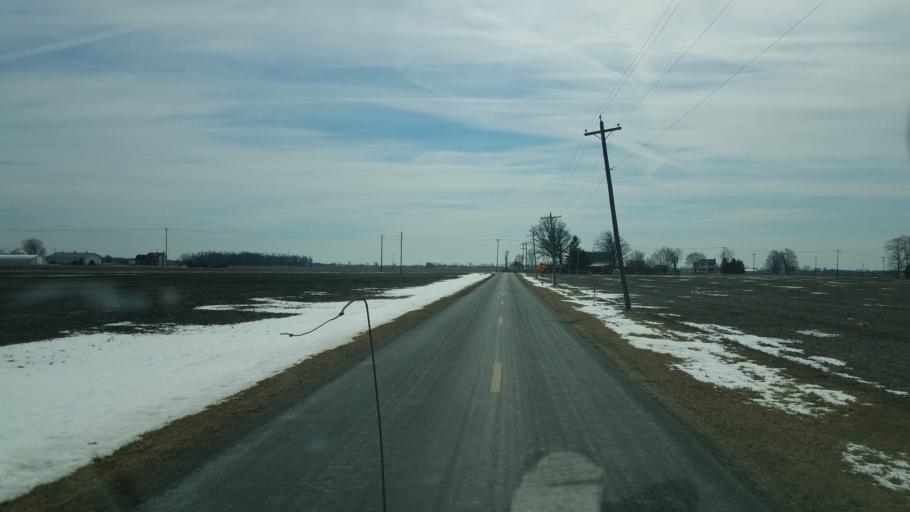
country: US
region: Ohio
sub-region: Delaware County
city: Delaware
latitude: 40.3352
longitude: -82.9980
